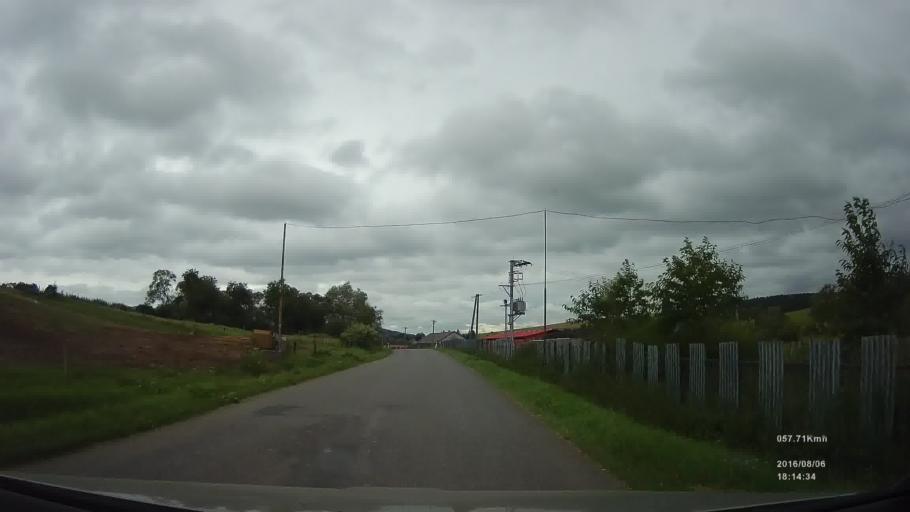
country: SK
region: Presovsky
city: Svidnik
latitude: 49.3522
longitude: 21.5953
